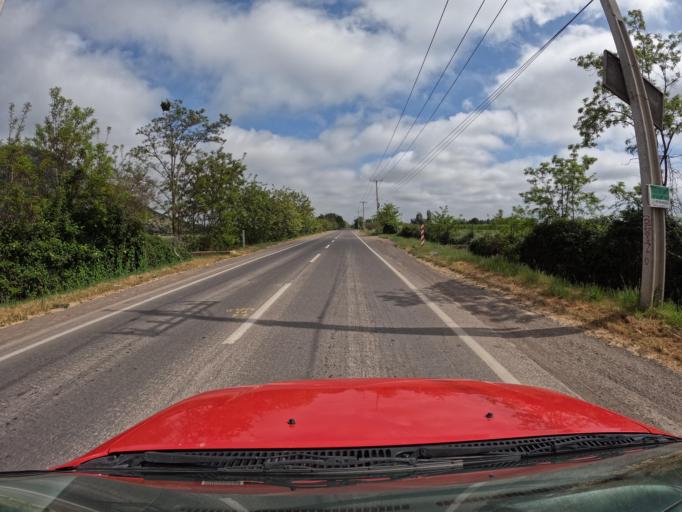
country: CL
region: O'Higgins
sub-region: Provincia de Colchagua
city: Santa Cruz
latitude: -34.7048
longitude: -71.3032
